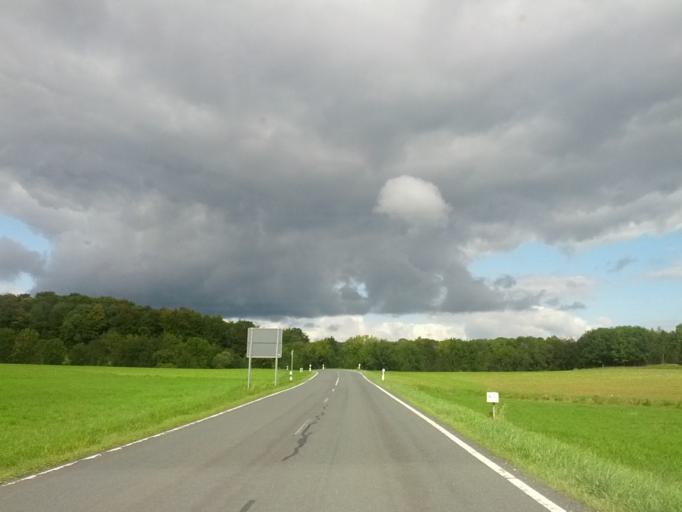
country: DE
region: Hesse
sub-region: Regierungsbezirk Kassel
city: Herleshausen
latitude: 51.0447
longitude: 10.1332
